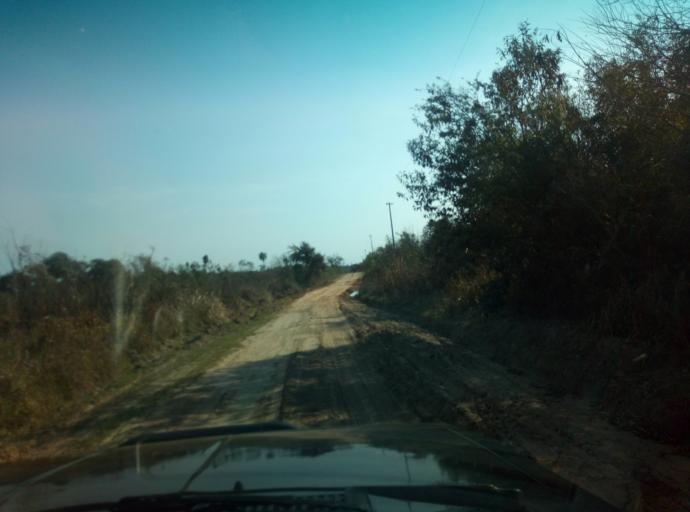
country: PY
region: Caaguazu
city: Doctor Cecilio Baez
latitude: -25.1868
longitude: -56.1918
